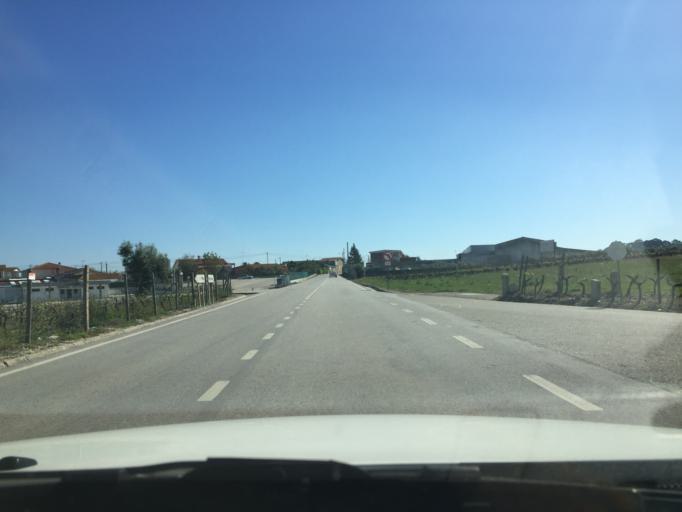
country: PT
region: Aveiro
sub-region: Anadia
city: Sangalhos
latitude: 40.4215
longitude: -8.5351
